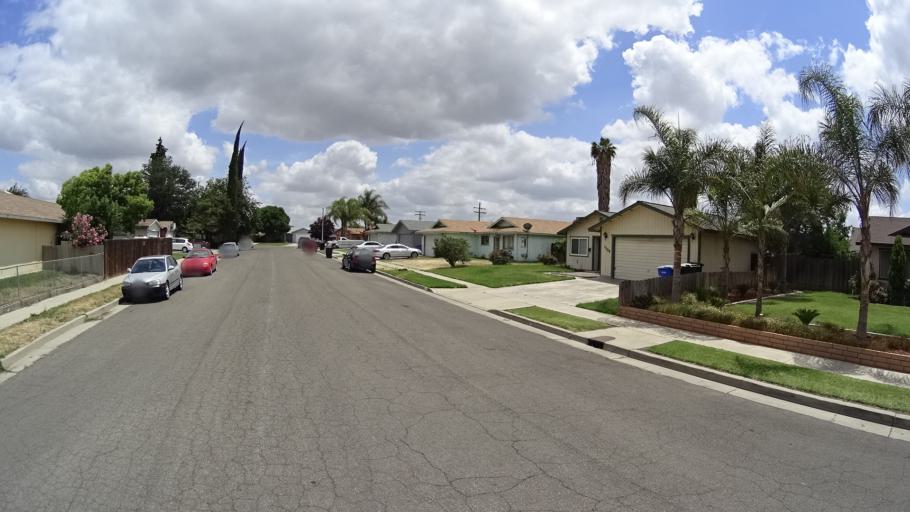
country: US
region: California
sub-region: Kings County
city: Hanford
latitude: 36.3101
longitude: -119.6712
